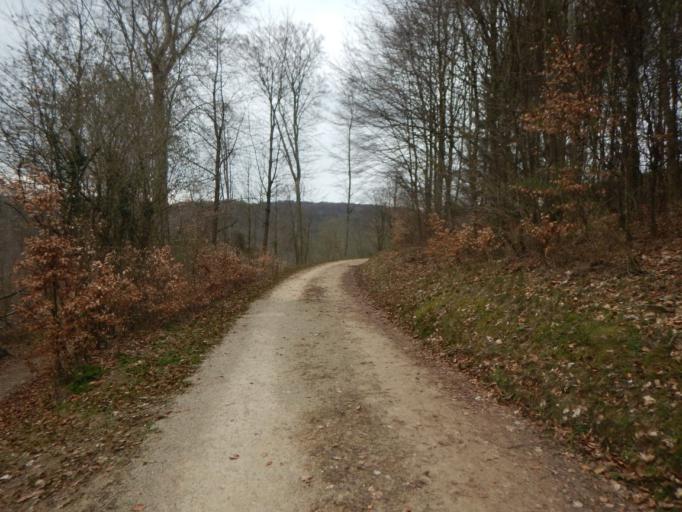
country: LU
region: Luxembourg
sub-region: Canton de Mersch
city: Lorentzweiler
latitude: 49.6988
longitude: 6.1519
